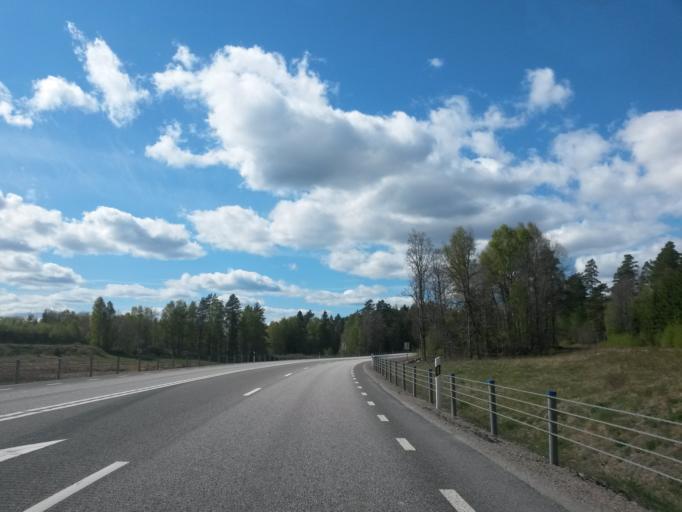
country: SE
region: Vaestra Goetaland
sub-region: Vargarda Kommun
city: Vargarda
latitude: 58.0464
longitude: 12.8631
